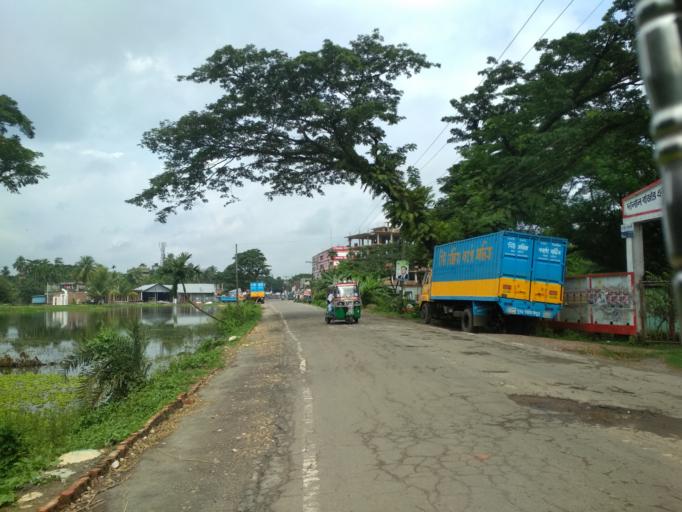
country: BD
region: Chittagong
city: Lakshmipur
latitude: 22.9682
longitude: 90.8093
